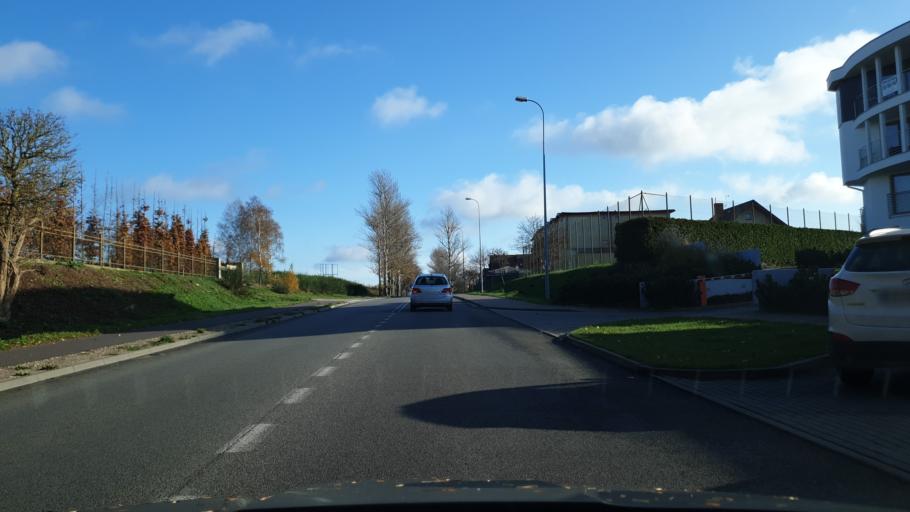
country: PL
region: Pomeranian Voivodeship
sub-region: Powiat pucki
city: Chlapowo
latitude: 54.8091
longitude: 18.3690
